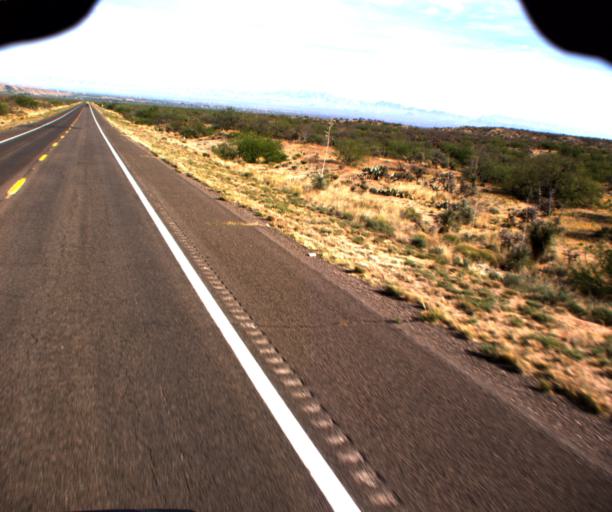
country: US
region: Arizona
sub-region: Graham County
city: Swift Trail Junction
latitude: 32.6323
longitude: -109.6920
